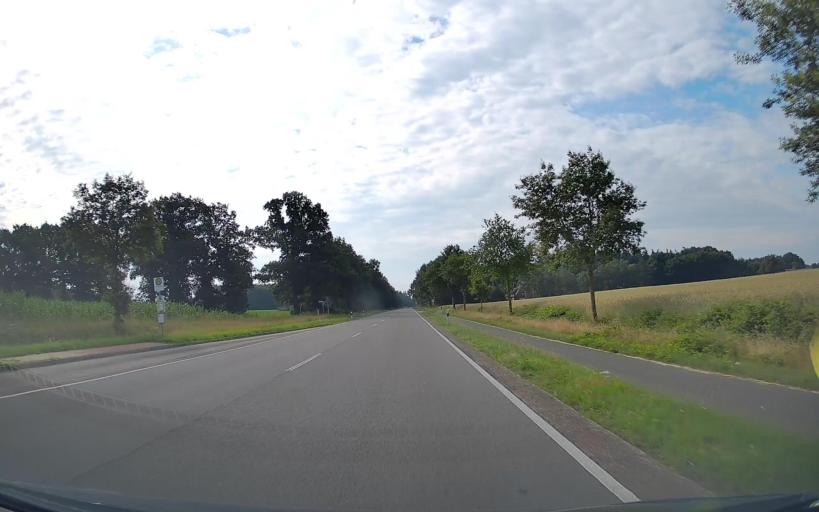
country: DE
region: Lower Saxony
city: Bosel
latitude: 52.9773
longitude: 7.9047
